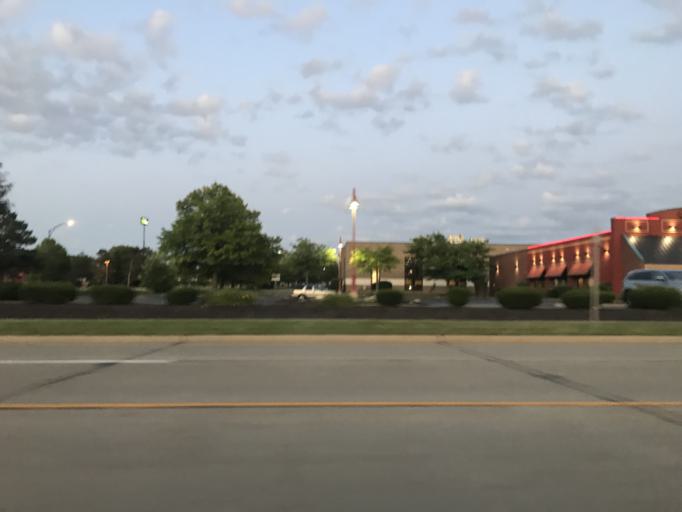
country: US
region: Ohio
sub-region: Cuyahoga County
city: Middleburg Heights
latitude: 41.3744
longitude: -81.8247
